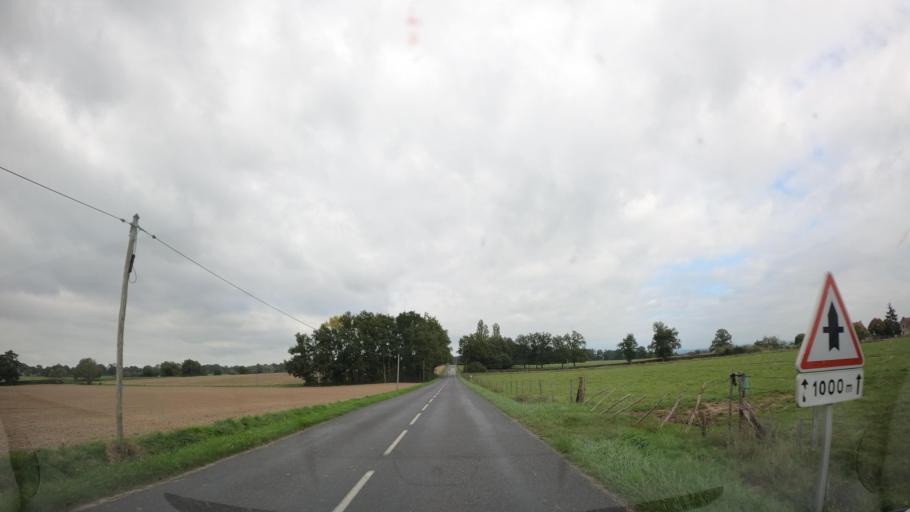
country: FR
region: Auvergne
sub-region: Departement de l'Allier
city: Saint-Gerand-le-Puy
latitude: 46.2723
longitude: 3.5463
